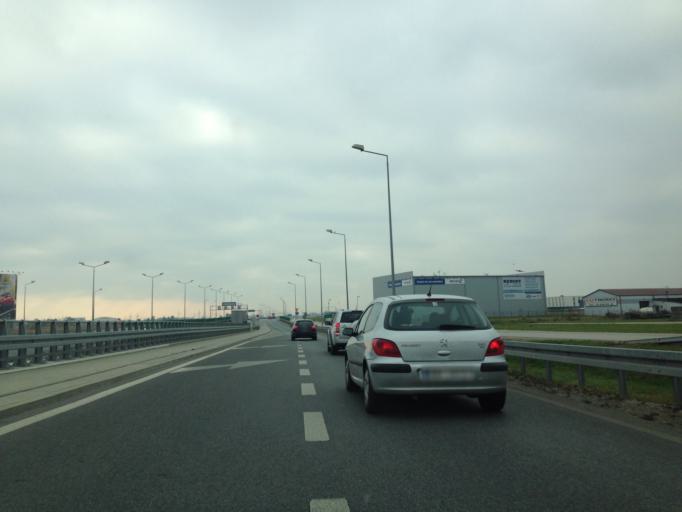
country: PL
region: Masovian Voivodeship
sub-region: Warszawa
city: Bemowo
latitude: 52.2398
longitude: 20.8881
